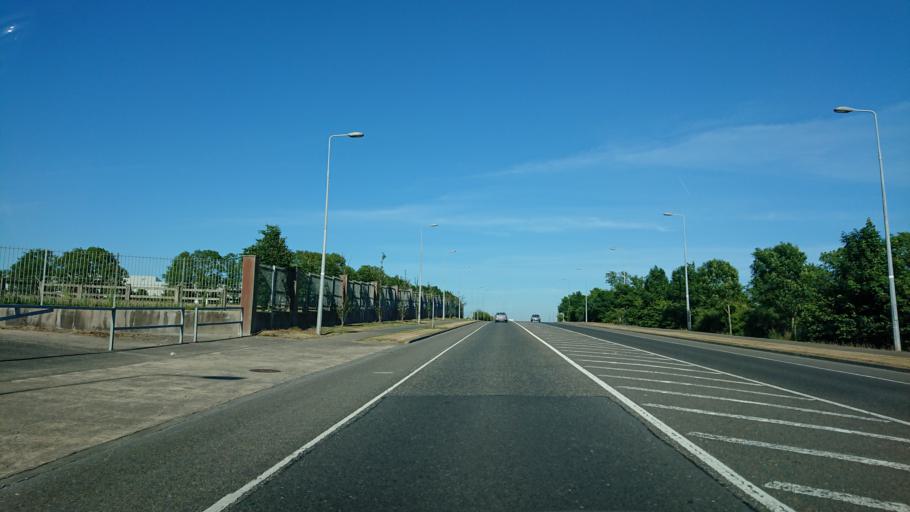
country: IE
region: Munster
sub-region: Waterford
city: Waterford
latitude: 52.2522
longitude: -7.1622
